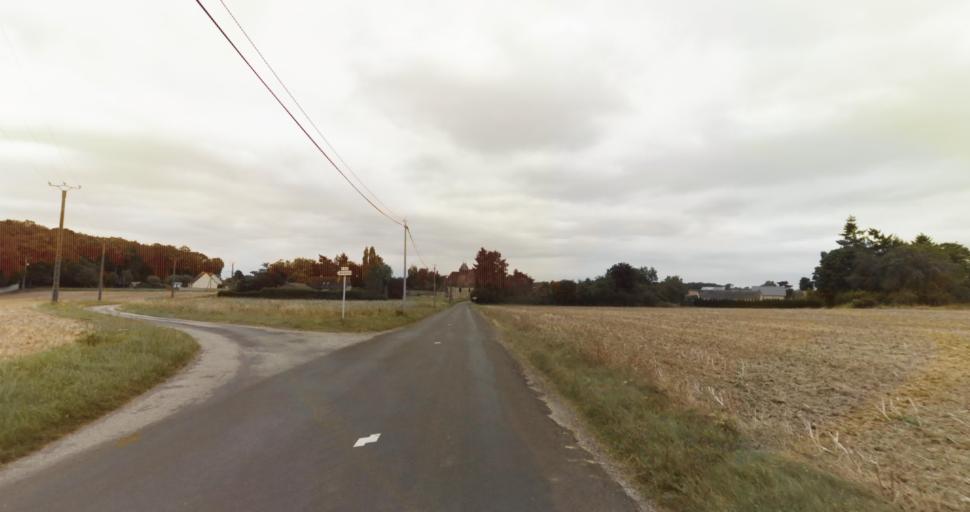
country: FR
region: Haute-Normandie
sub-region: Departement de l'Eure
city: La Couture-Boussey
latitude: 48.8982
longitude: 1.3588
